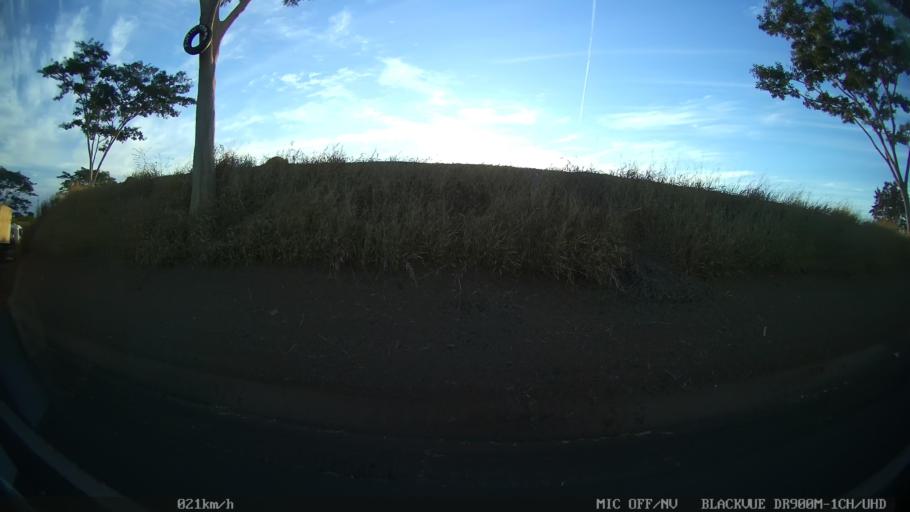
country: BR
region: Sao Paulo
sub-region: Catanduva
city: Catanduva
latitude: -21.1340
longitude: -49.0188
